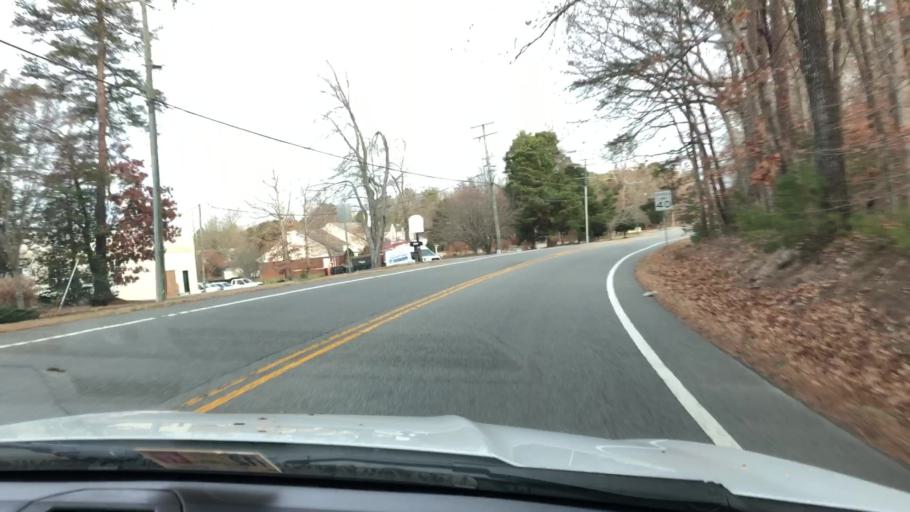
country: US
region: Virginia
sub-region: James City County
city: Williamsburg
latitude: 37.2654
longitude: -76.7411
